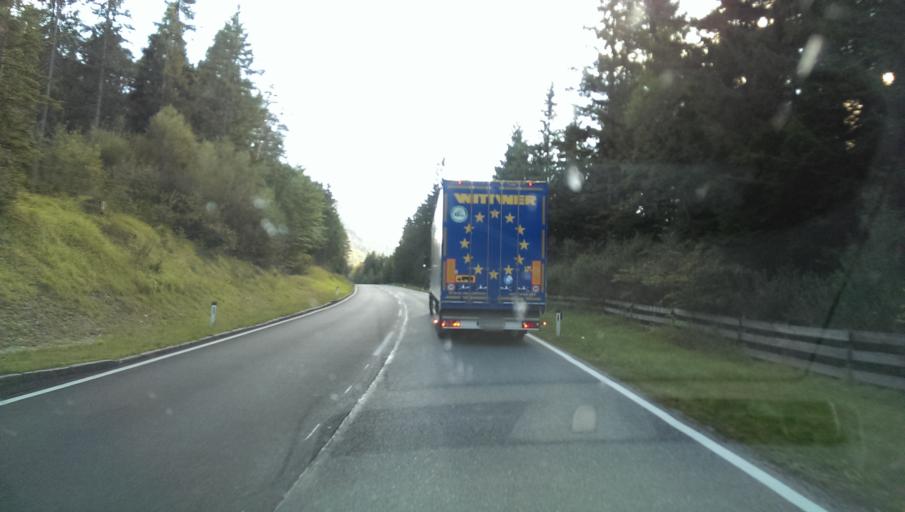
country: AT
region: Tyrol
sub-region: Politischer Bezirk Innsbruck Land
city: Seefeld in Tirol
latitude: 47.3566
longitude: 11.2244
